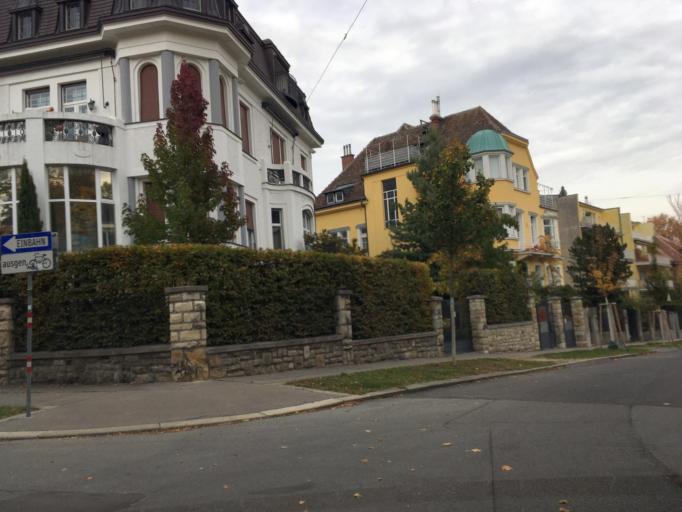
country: AT
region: Vienna
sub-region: Wien Stadt
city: Vienna
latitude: 48.2360
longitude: 16.3388
